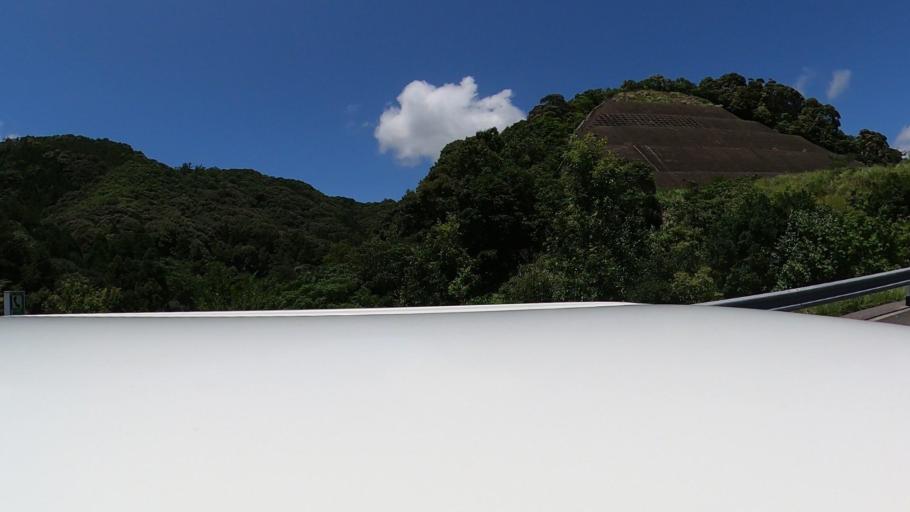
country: JP
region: Miyazaki
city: Nobeoka
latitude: 32.4784
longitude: 131.6309
